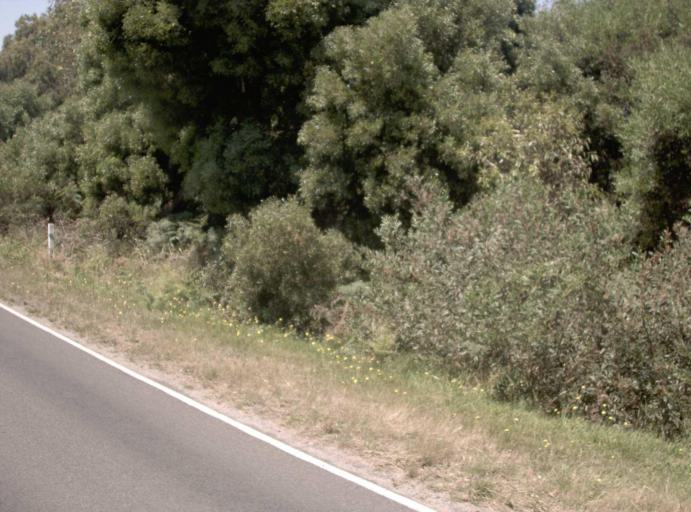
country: AU
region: Victoria
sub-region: Bass Coast
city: North Wonthaggi
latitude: -38.6750
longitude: 145.8645
